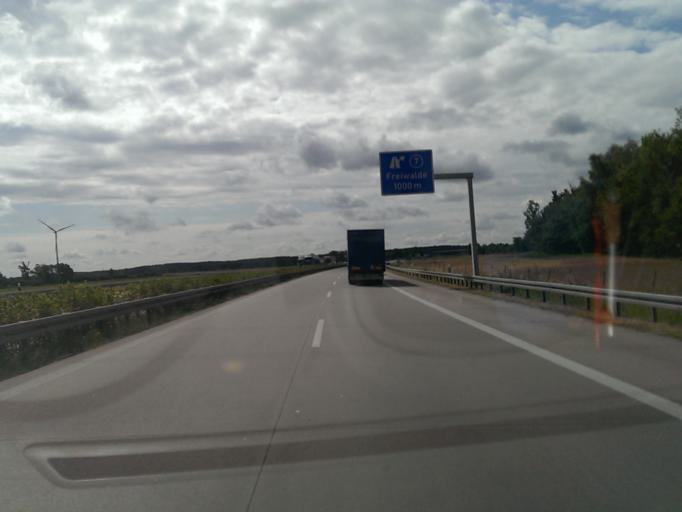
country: DE
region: Brandenburg
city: Kasel-Golzig
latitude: 51.9669
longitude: 13.7604
